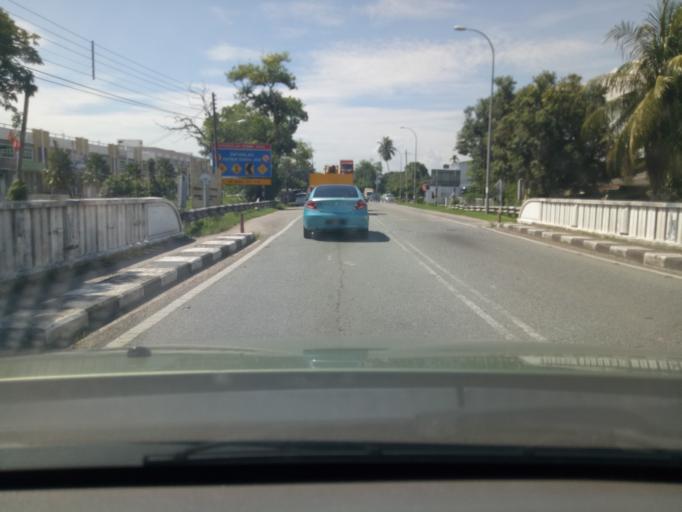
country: MY
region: Kedah
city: Alor Setar
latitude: 5.9704
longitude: 100.4014
